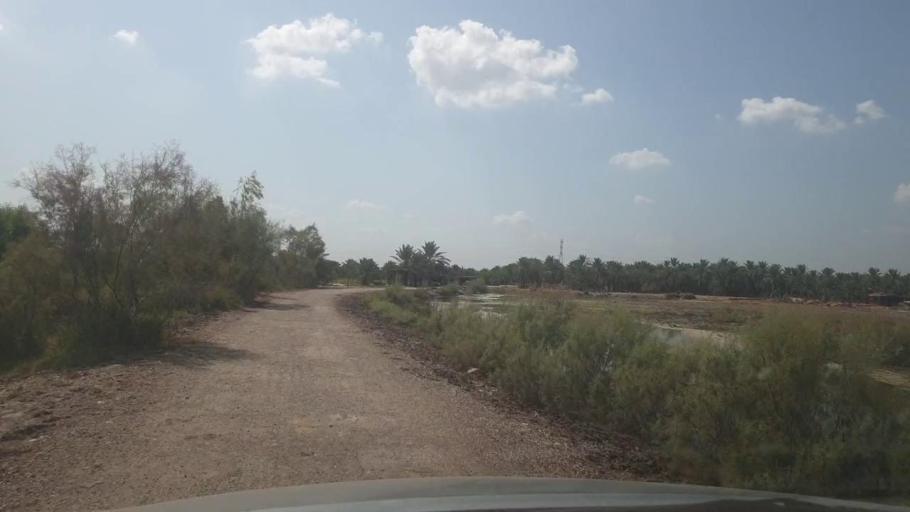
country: PK
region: Sindh
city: Khairpur
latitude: 27.5490
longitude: 68.8140
